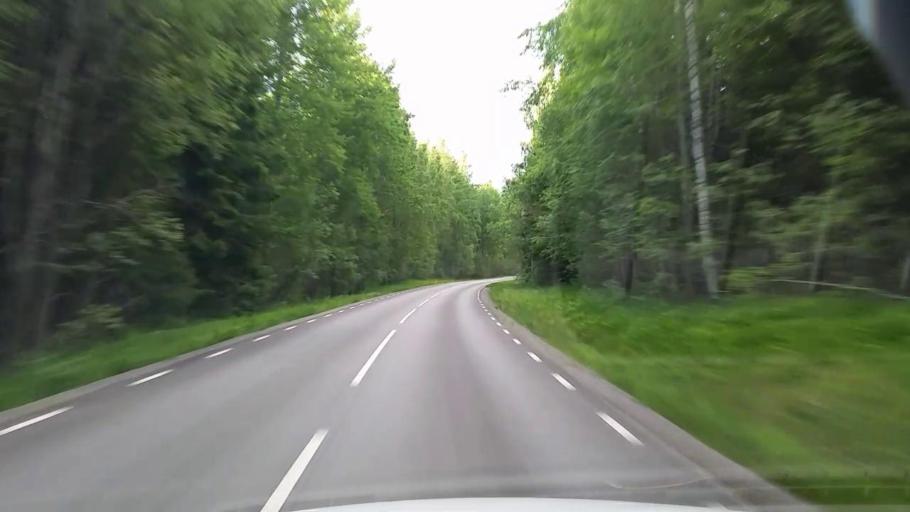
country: SE
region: Vaestmanland
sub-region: Kopings Kommun
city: Kolsva
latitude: 59.7168
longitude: 15.8299
